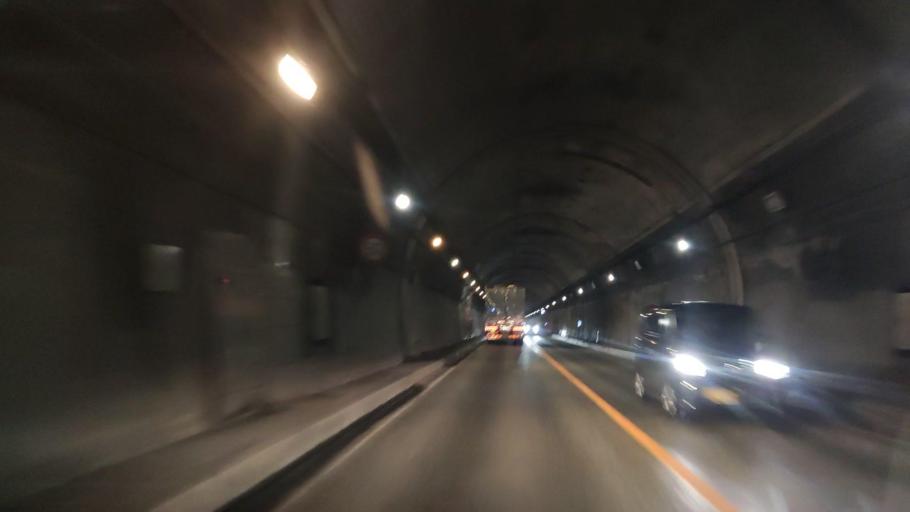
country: JP
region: Aomori
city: Aomori Shi
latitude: 40.7773
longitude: 140.9629
